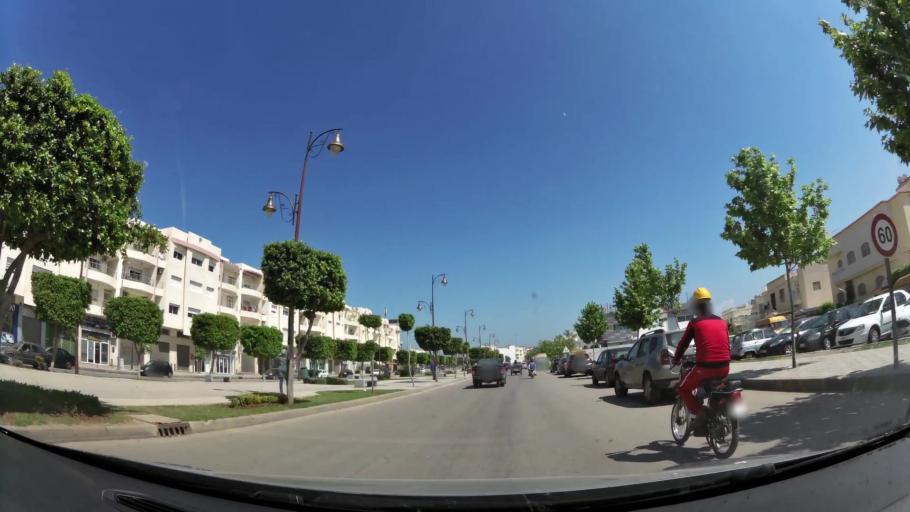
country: MA
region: Fes-Boulemane
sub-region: Fes
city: Fes
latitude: 34.0198
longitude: -5.0238
